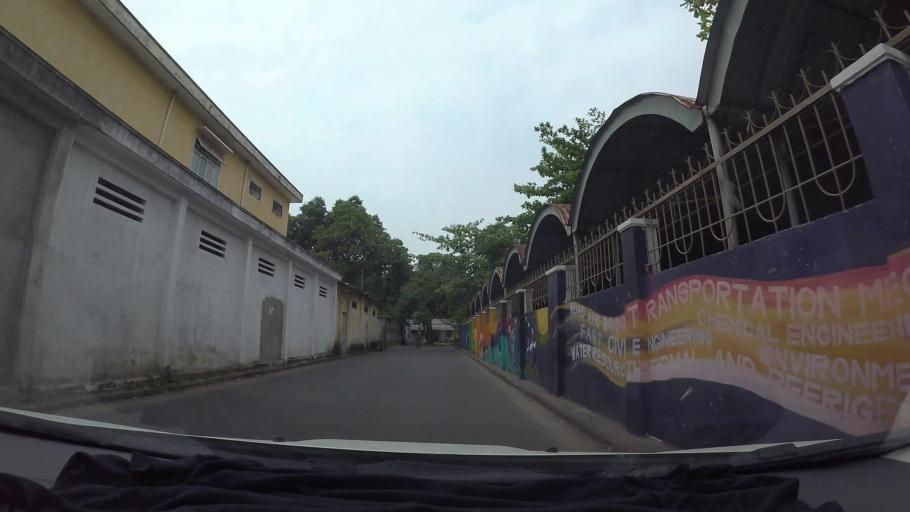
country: VN
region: Da Nang
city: Lien Chieu
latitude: 16.0741
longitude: 108.1522
